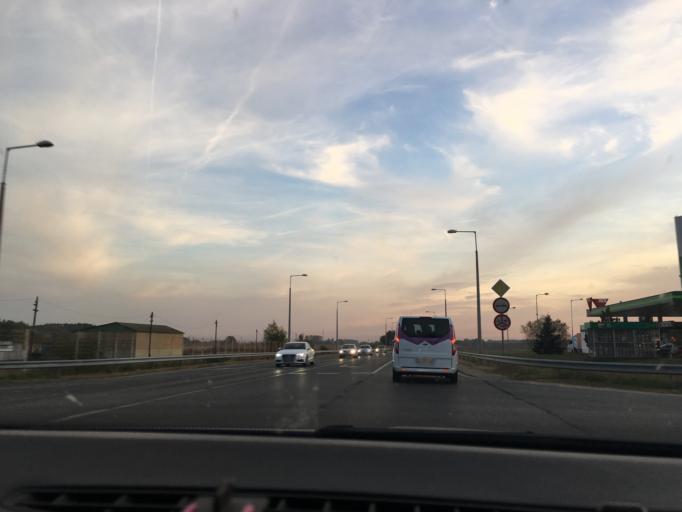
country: HU
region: Hajdu-Bihar
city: Teglas
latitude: 47.7095
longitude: 21.6594
